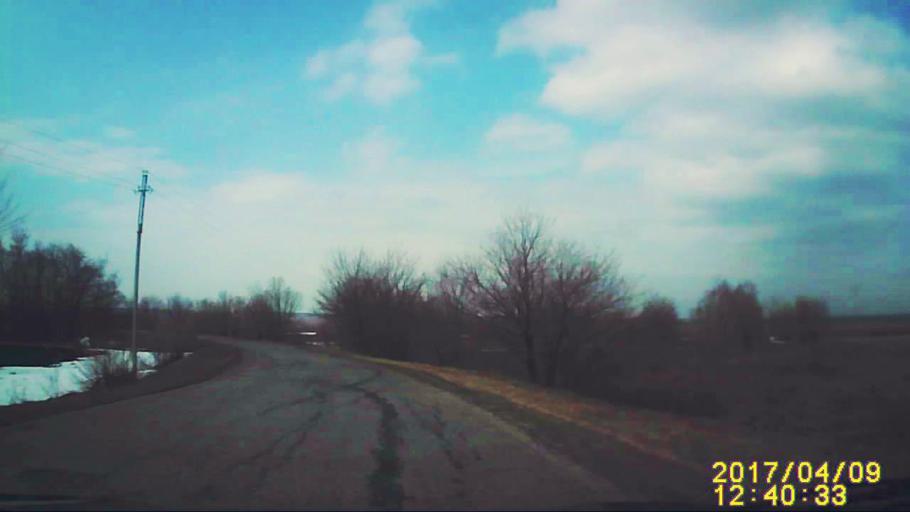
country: RU
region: Ulyanovsk
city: Ignatovka
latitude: 54.0035
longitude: 47.9451
